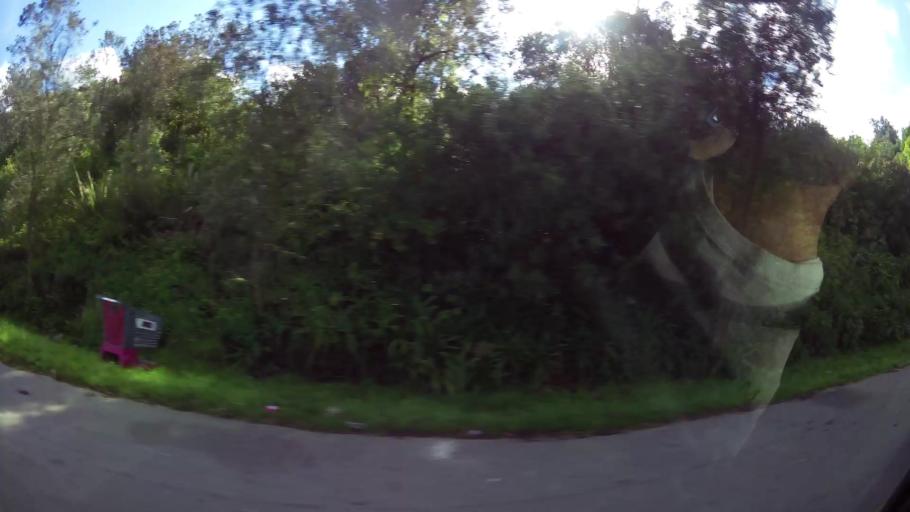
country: ZA
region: Western Cape
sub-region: Eden District Municipality
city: Knysna
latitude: -34.0380
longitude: 23.0616
